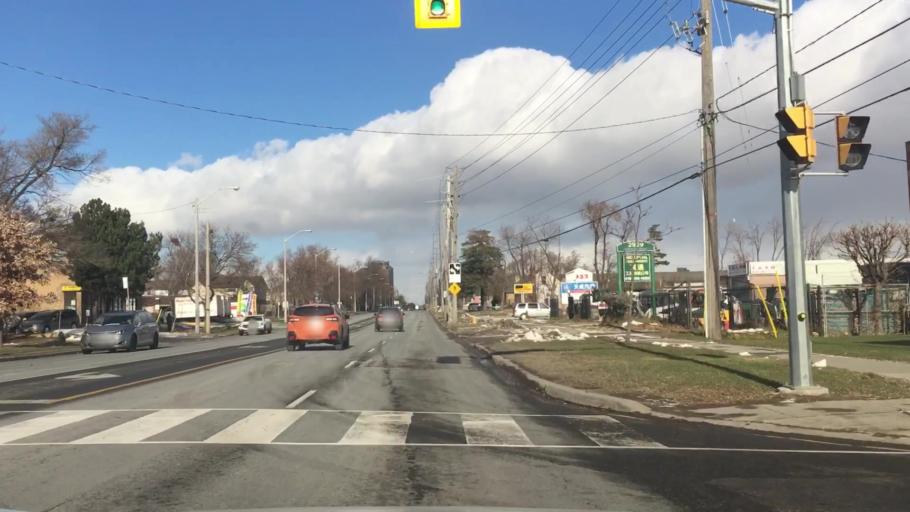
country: CA
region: Ontario
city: Scarborough
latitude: 43.8040
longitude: -79.2982
